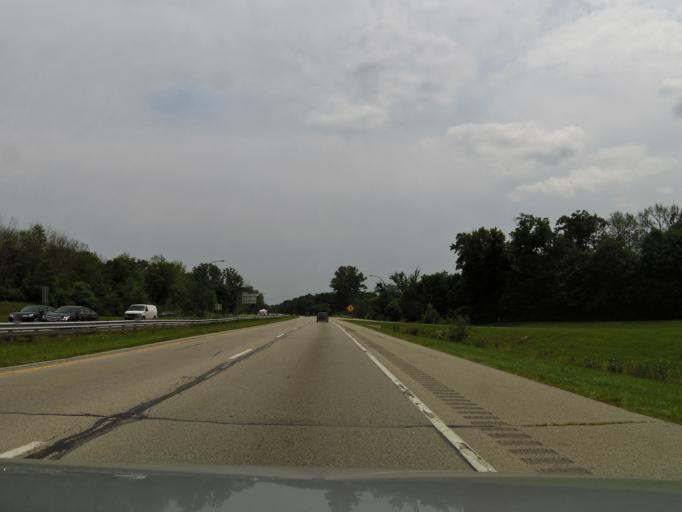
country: US
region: Ohio
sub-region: Greene County
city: Beavercreek
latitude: 39.7196
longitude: -84.0581
